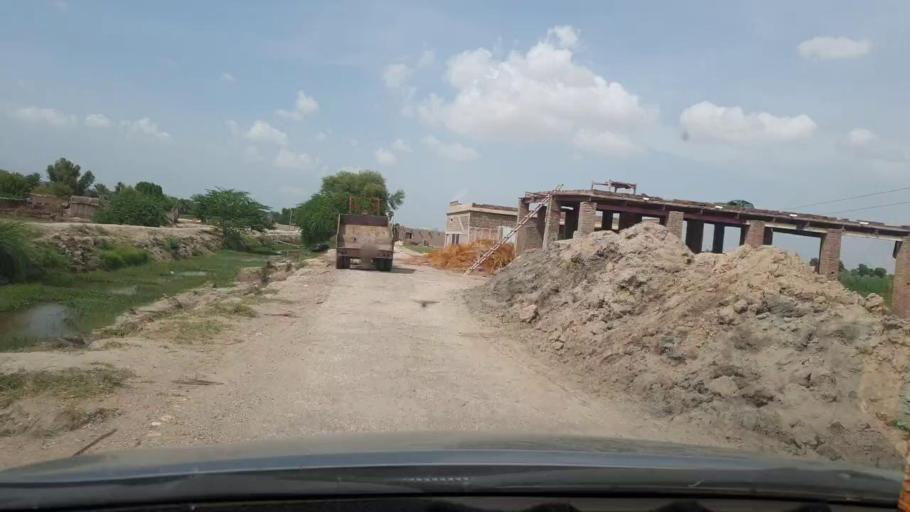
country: PK
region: Sindh
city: Khairpur
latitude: 27.5244
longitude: 68.8852
